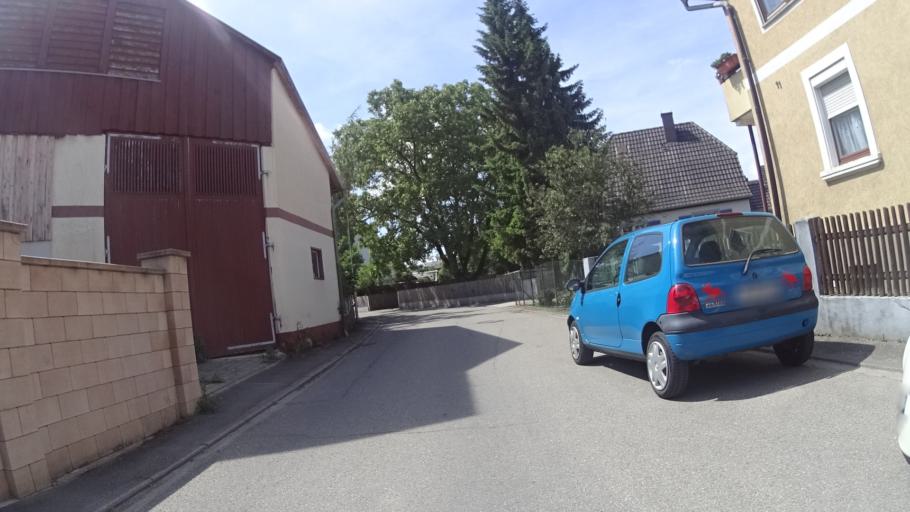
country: DE
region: Baden-Wuerttemberg
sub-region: Freiburg Region
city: Meissenheim
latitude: 48.4130
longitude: 7.7761
